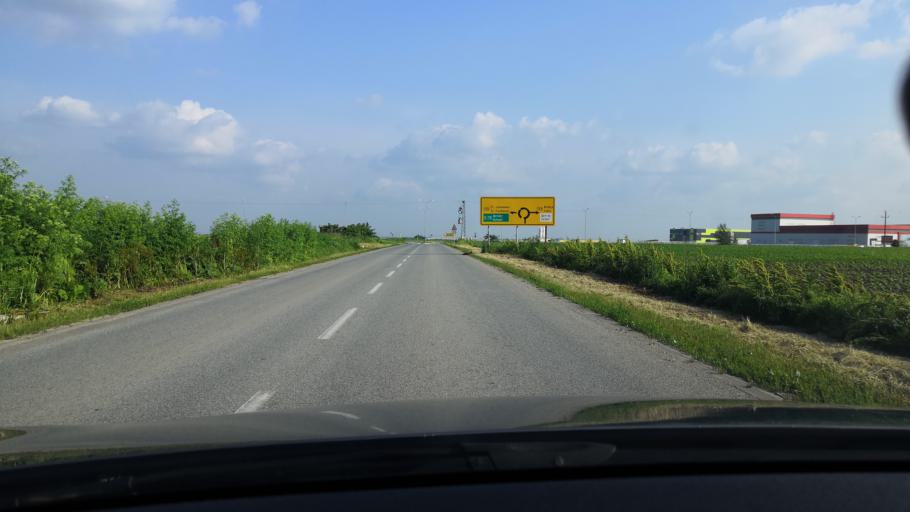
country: RS
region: Autonomna Pokrajina Vojvodina
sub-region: Sremski Okrug
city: Ingija
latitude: 45.0663
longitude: 20.1275
